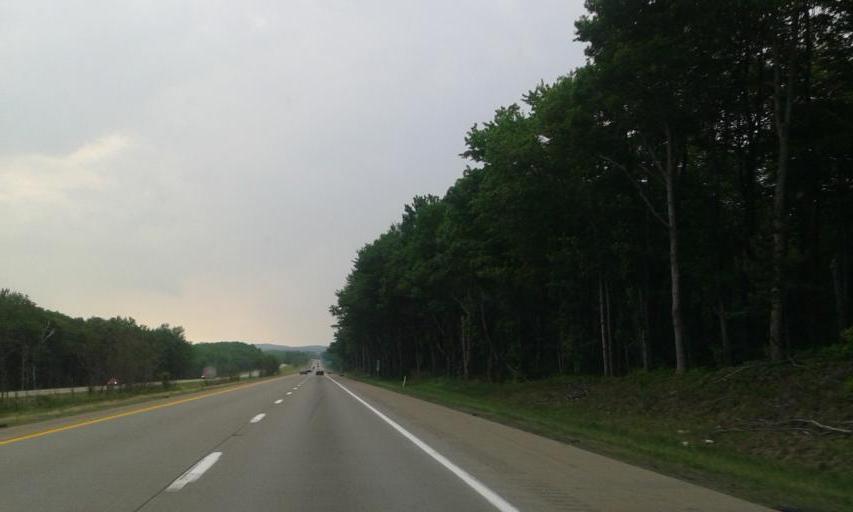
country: US
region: Pennsylvania
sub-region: Monroe County
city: Pocono Pines
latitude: 41.2140
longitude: -75.4730
